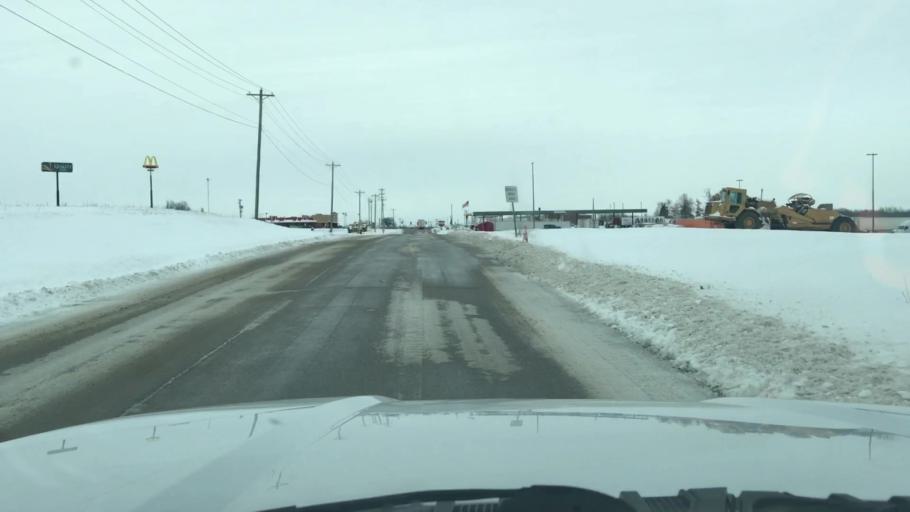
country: US
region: Missouri
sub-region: Clinton County
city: Cameron
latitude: 39.7493
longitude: -94.2153
